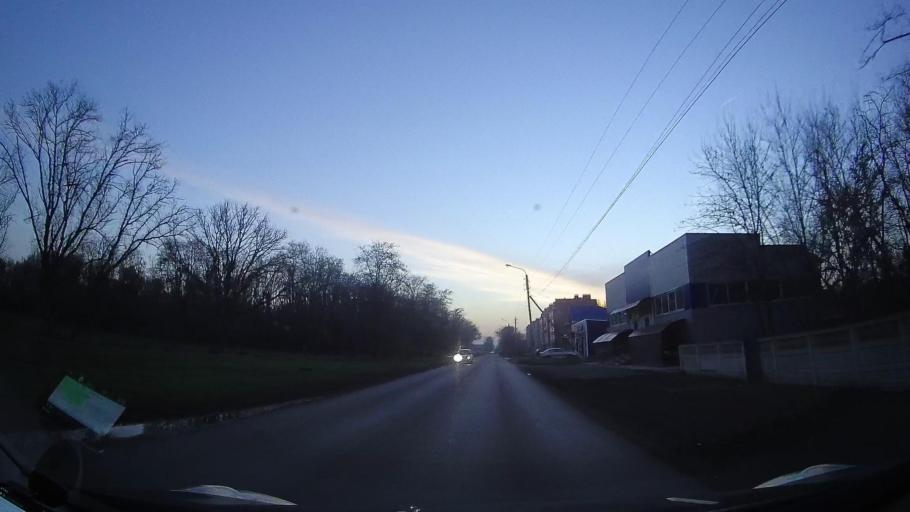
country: RU
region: Rostov
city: Zernograd
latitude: 46.8558
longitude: 40.3169
